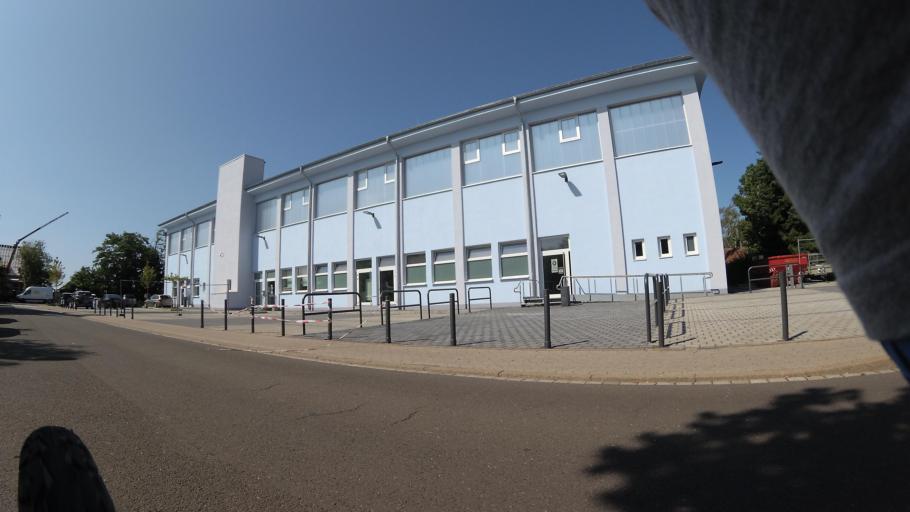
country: DE
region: Saarland
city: Saarbrucken
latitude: 49.2277
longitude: 6.9752
